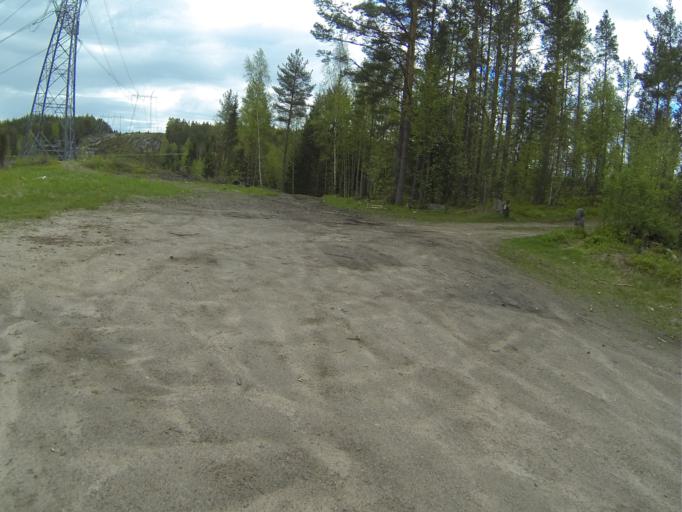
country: FI
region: Varsinais-Suomi
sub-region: Salo
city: Halikko
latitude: 60.3413
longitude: 23.0871
